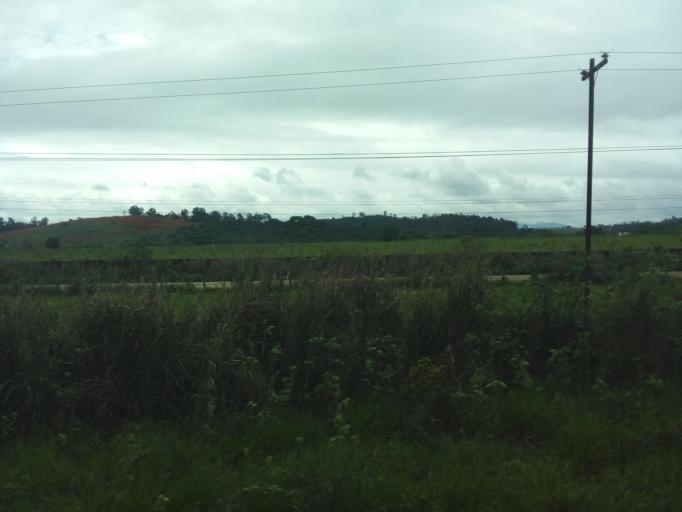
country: BR
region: Minas Gerais
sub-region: Ipatinga
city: Ipatinga
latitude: -19.4673
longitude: -42.4784
